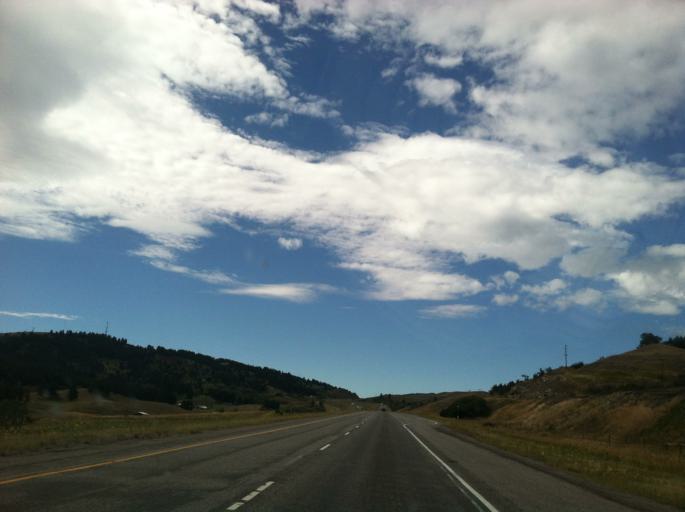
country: US
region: Montana
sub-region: Park County
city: Livingston
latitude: 45.6575
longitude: -110.7793
